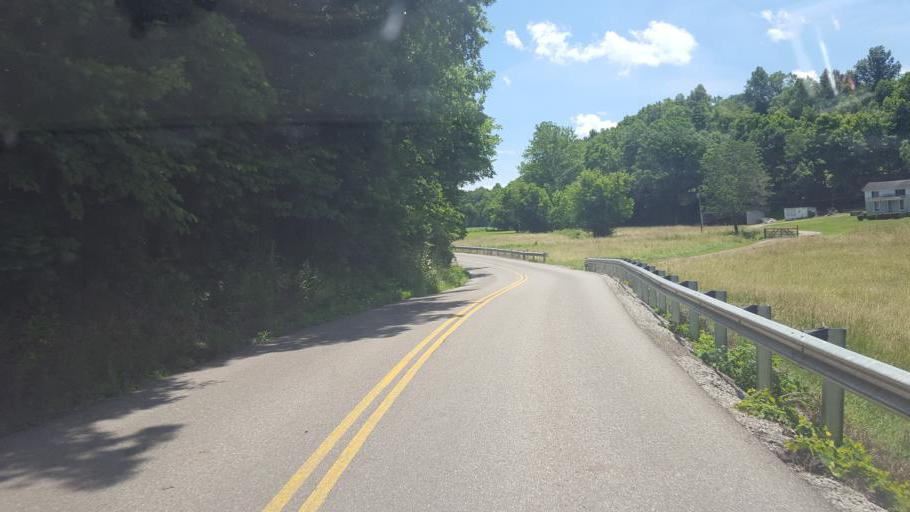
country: US
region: Ohio
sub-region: Gallia County
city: Gallipolis
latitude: 38.7246
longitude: -82.3617
